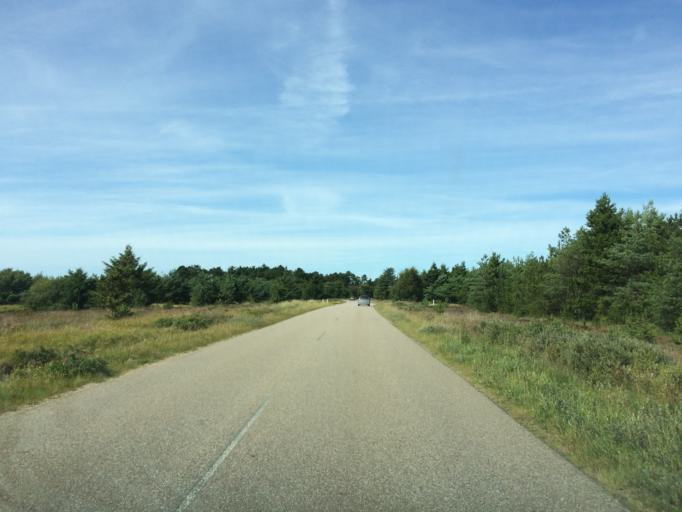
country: DK
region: South Denmark
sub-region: Varde Kommune
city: Oksbol
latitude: 55.6703
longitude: 8.1915
